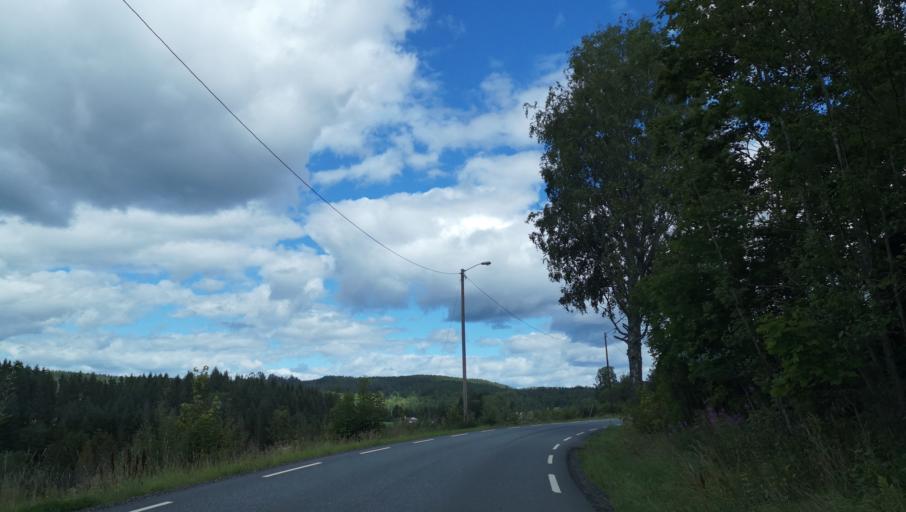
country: NO
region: Ostfold
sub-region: Hobol
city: Tomter
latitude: 59.6668
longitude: 11.0022
